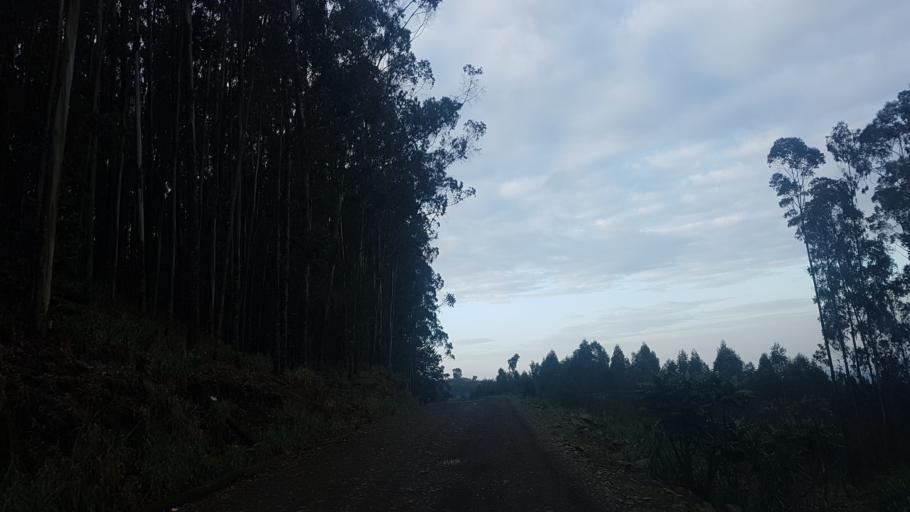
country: ET
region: Amhara
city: Finote Selam
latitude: 10.7919
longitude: 37.6641
